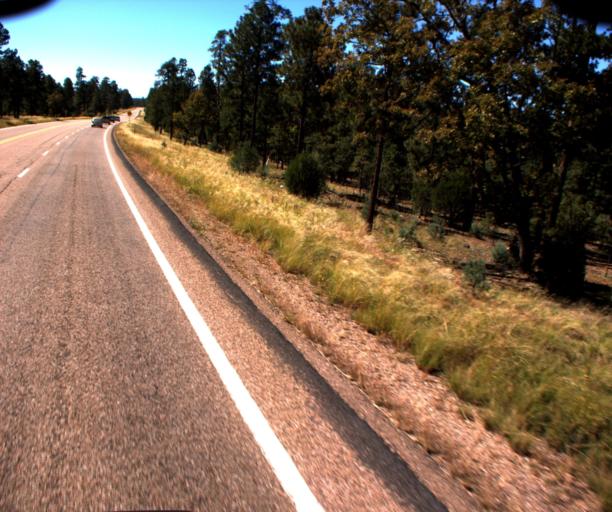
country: US
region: Arizona
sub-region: Navajo County
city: Heber-Overgaard
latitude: 34.3764
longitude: -110.6766
